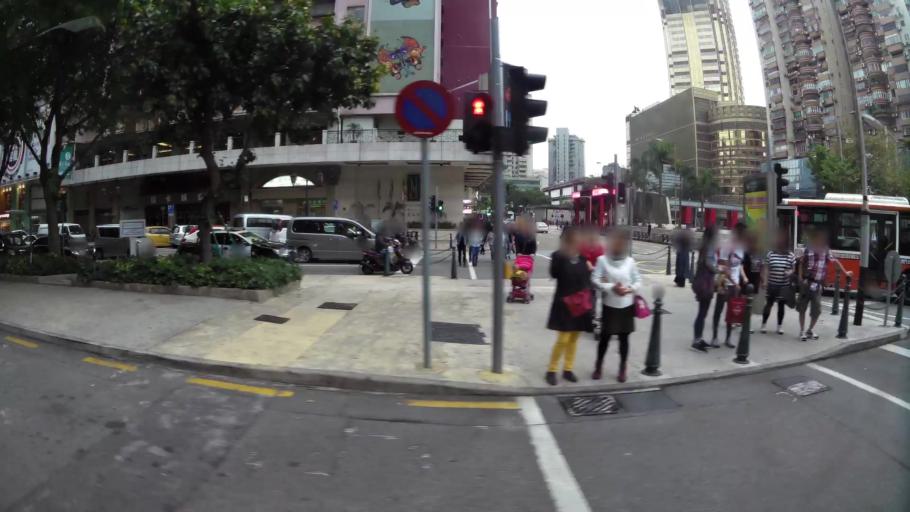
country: MO
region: Macau
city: Macau
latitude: 22.1907
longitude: 113.5412
